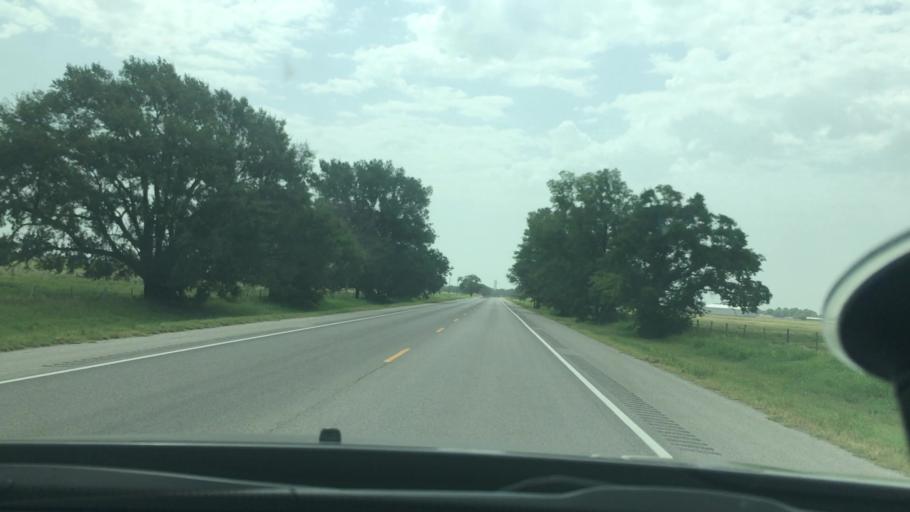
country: US
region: Oklahoma
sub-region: Garvin County
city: Pauls Valley
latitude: 34.8404
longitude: -97.2719
